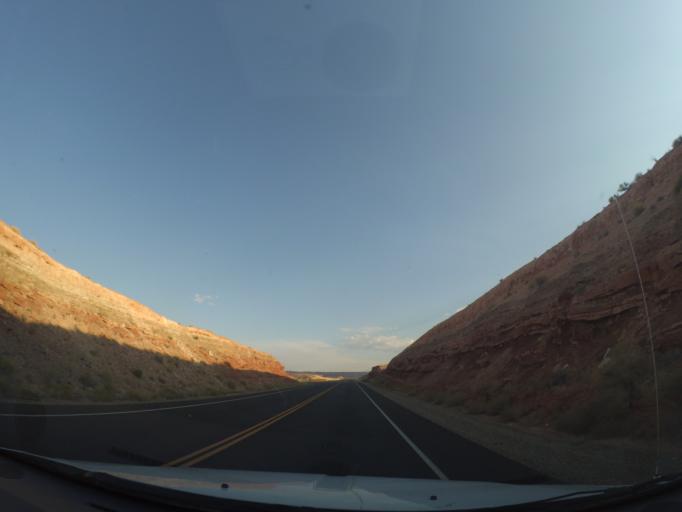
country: US
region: Arizona
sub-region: Coconino County
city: Page
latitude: 36.9721
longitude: -111.4908
